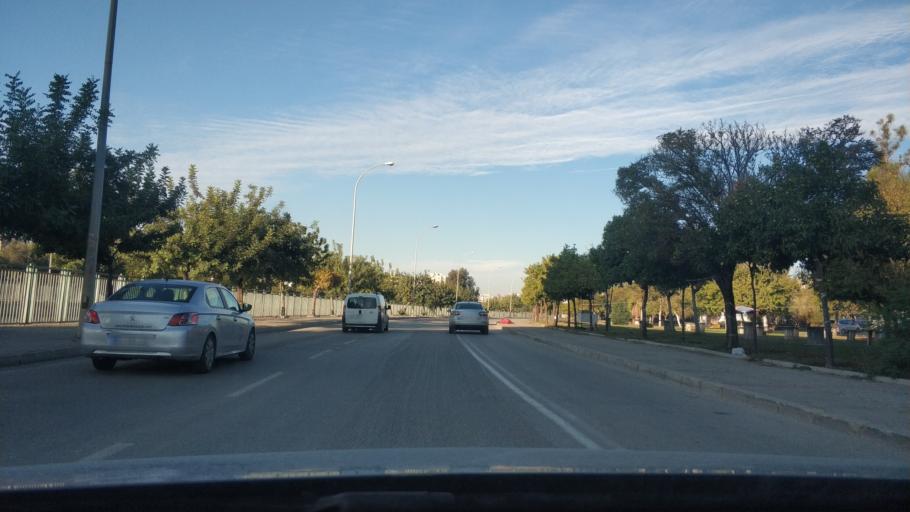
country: TR
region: Adana
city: Seyhan
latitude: 37.0107
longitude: 35.2877
